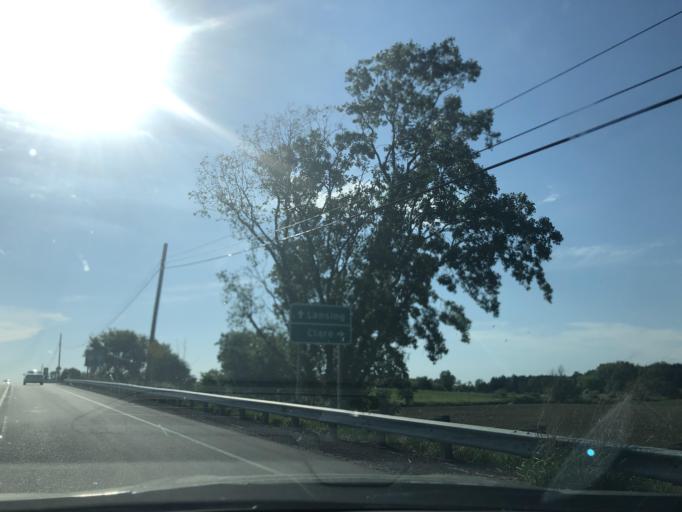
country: US
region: Michigan
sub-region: Isabella County
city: Shepherd
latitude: 43.5241
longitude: -84.6744
